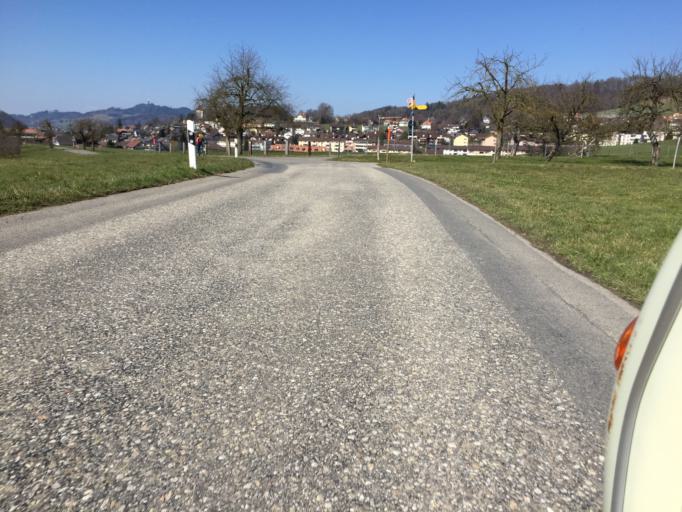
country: CH
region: Bern
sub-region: Bern-Mittelland District
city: Worb
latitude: 46.9214
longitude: 7.5738
